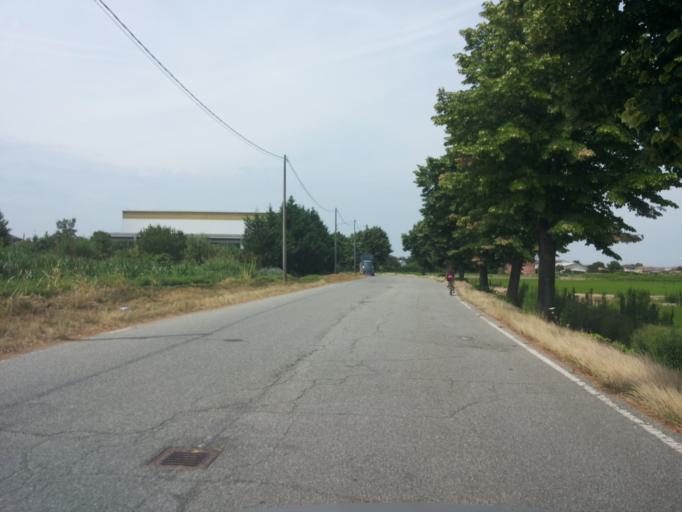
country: IT
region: Piedmont
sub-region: Provincia di Vercelli
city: Pezzana
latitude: 45.2648
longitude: 8.4937
